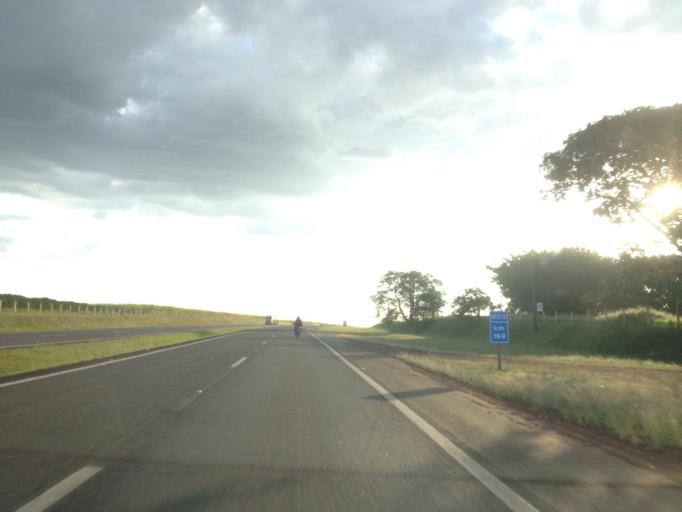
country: BR
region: Sao Paulo
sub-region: Jau
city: Jau
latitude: -22.2706
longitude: -48.4675
